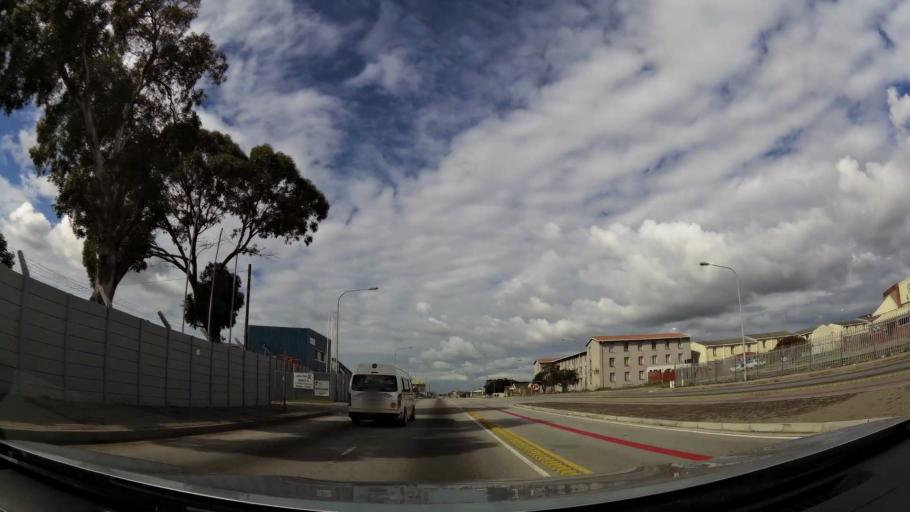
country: ZA
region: Eastern Cape
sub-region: Nelson Mandela Bay Metropolitan Municipality
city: Port Elizabeth
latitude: -33.9283
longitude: 25.5744
